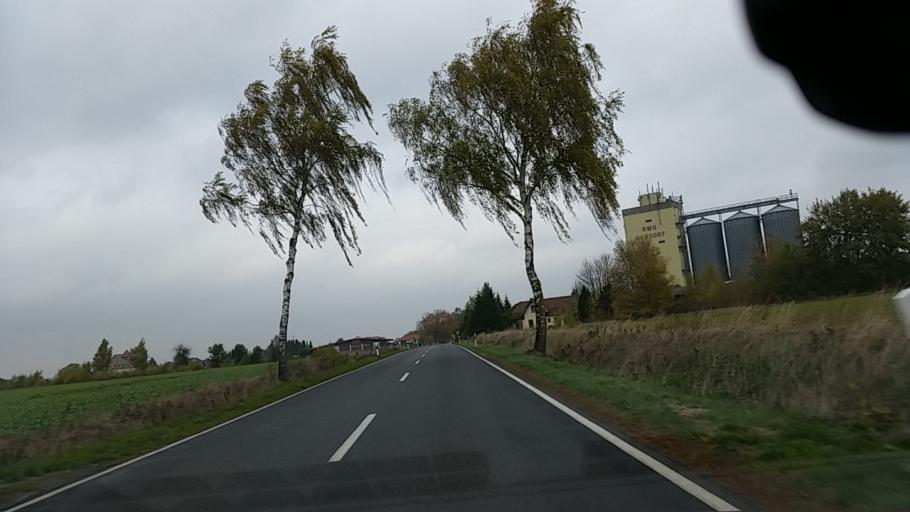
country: DE
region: Lower Saxony
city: Wittingen
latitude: 52.6906
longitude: 10.8077
